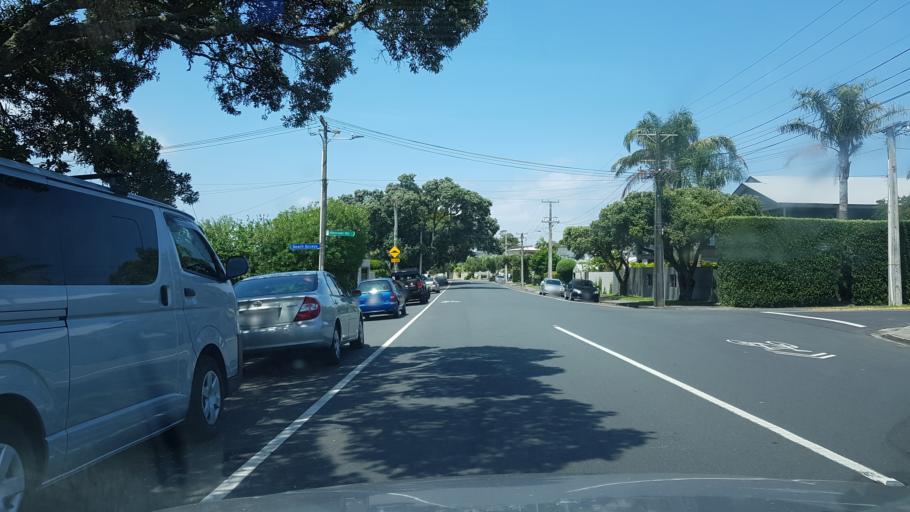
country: NZ
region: Auckland
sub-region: Auckland
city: North Shore
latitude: -36.8041
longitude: 174.7933
